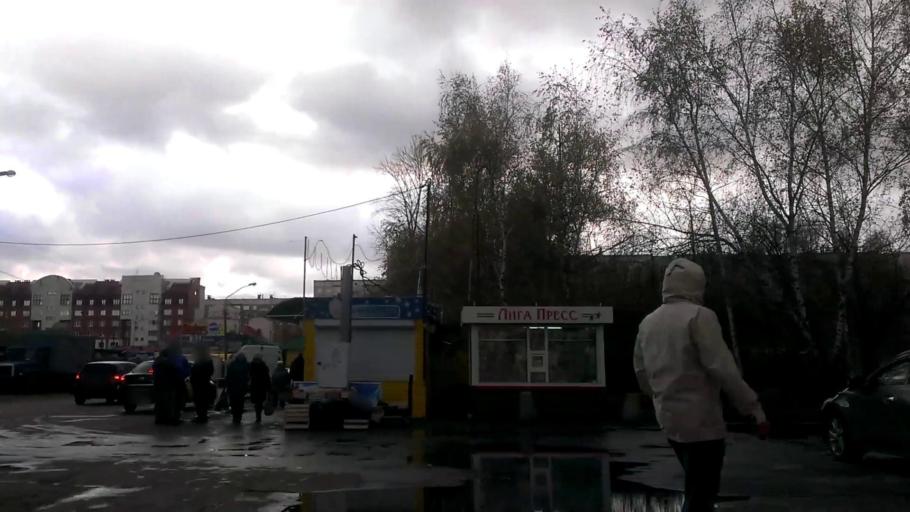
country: RU
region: Altai Krai
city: Novosilikatnyy
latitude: 53.3453
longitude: 83.6751
